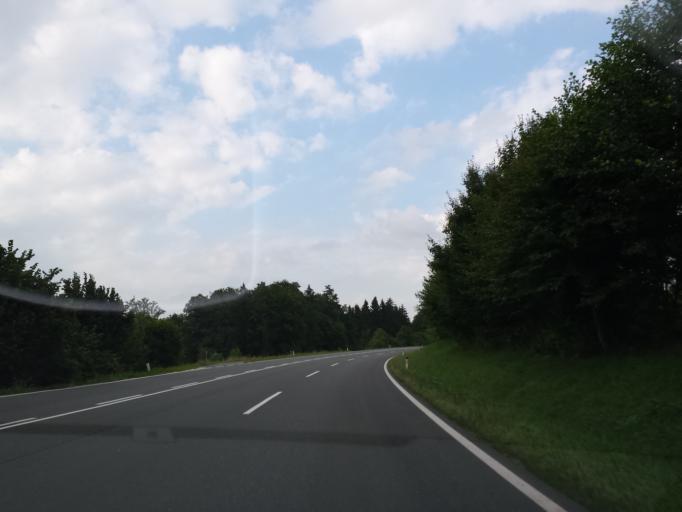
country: AT
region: Styria
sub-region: Politischer Bezirk Deutschlandsberg
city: Lannach
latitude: 46.9342
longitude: 15.3152
